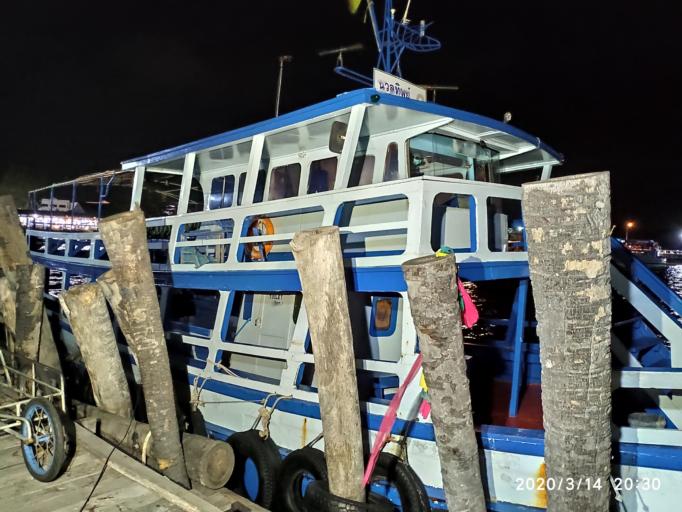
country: TH
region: Rayong
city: Rayong
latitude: 12.6264
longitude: 101.4425
